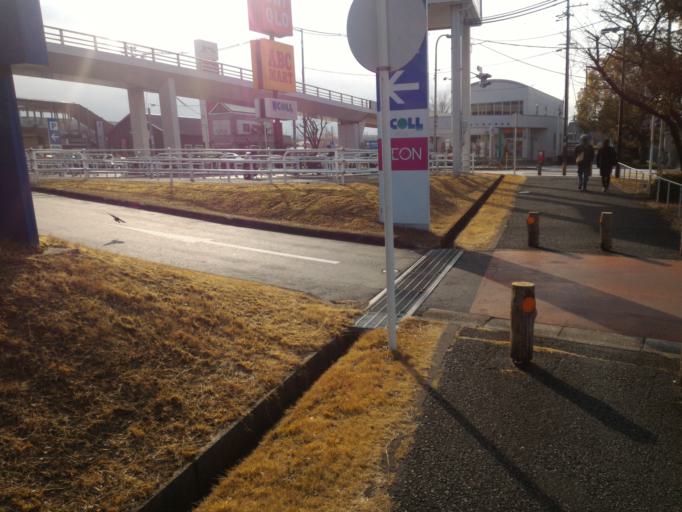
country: JP
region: Osaka
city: Tondabayashicho
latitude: 34.5012
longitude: 135.5788
